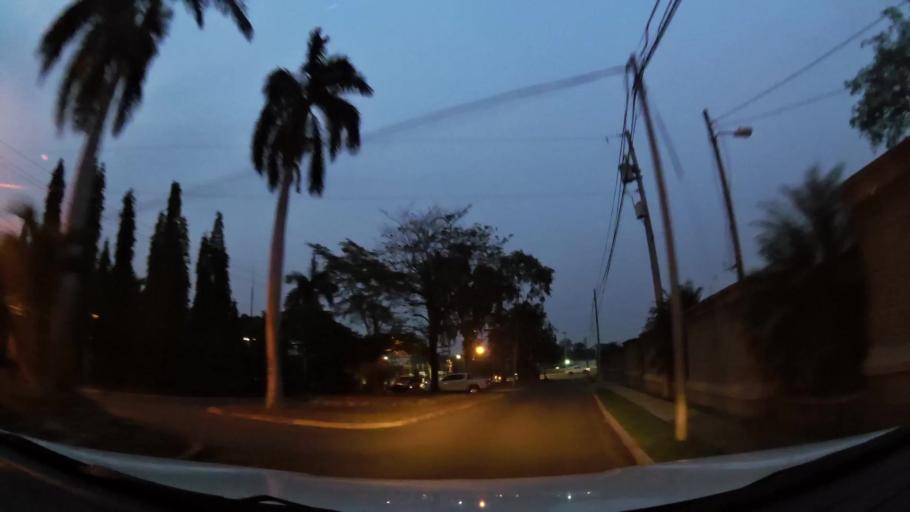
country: NI
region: Masaya
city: Ticuantepe
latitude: 12.0416
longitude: -86.1913
